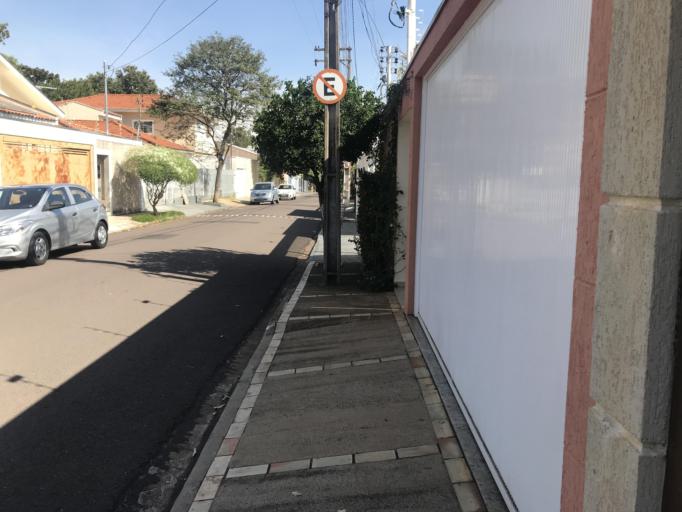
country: BR
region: Sao Paulo
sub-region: Presidente Prudente
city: Presidente Prudente
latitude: -22.1207
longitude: -51.4094
